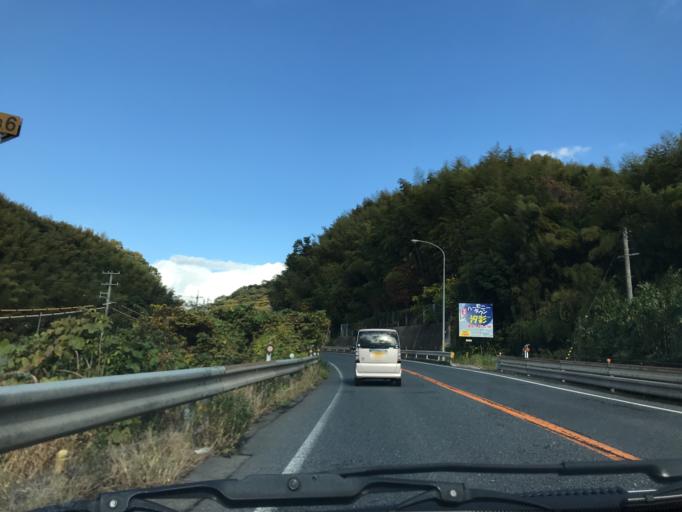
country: JP
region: Shimane
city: Yasugicho
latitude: 35.4209
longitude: 133.2881
